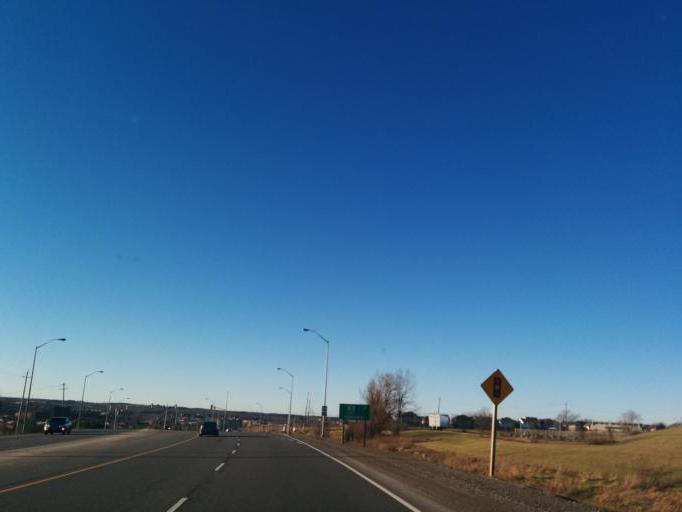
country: CA
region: Ontario
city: Orangeville
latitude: 43.9184
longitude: -80.0752
